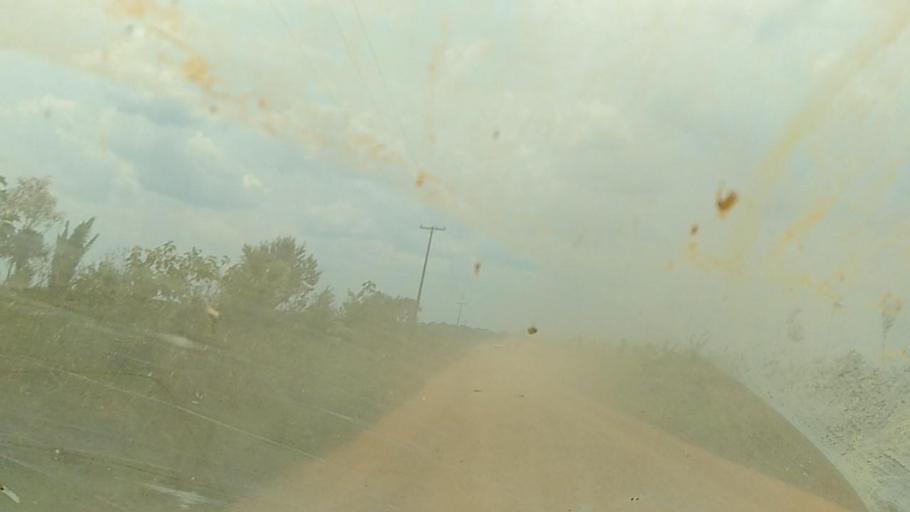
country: BR
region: Rondonia
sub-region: Porto Velho
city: Porto Velho
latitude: -8.9411
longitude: -64.3050
